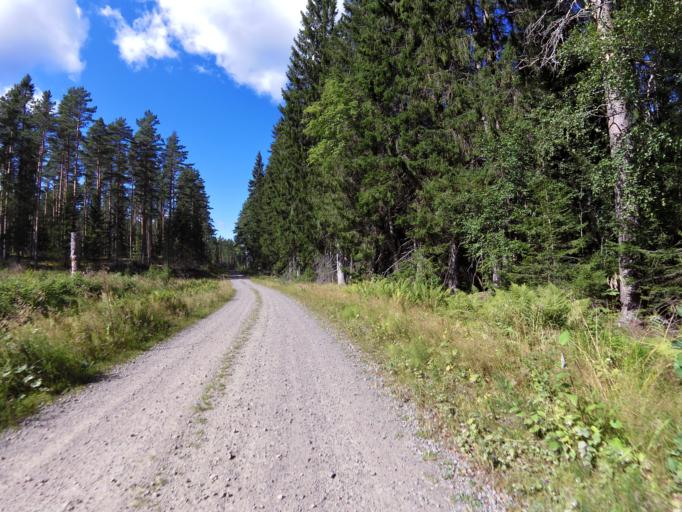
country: SE
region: Gaevleborg
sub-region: Ockelbo Kommun
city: Ockelbo
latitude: 60.8068
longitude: 16.7978
